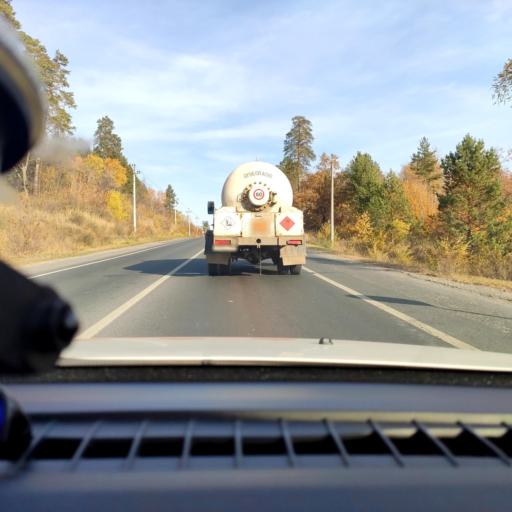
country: RU
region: Samara
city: Volzhskiy
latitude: 53.4437
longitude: 50.1233
